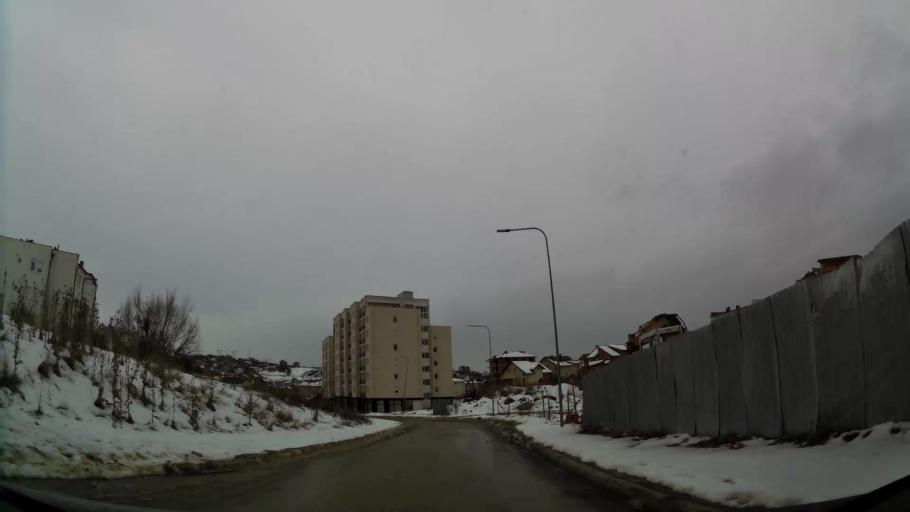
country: XK
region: Pristina
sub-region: Komuna e Prishtines
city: Pristina
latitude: 42.6446
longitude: 21.1823
